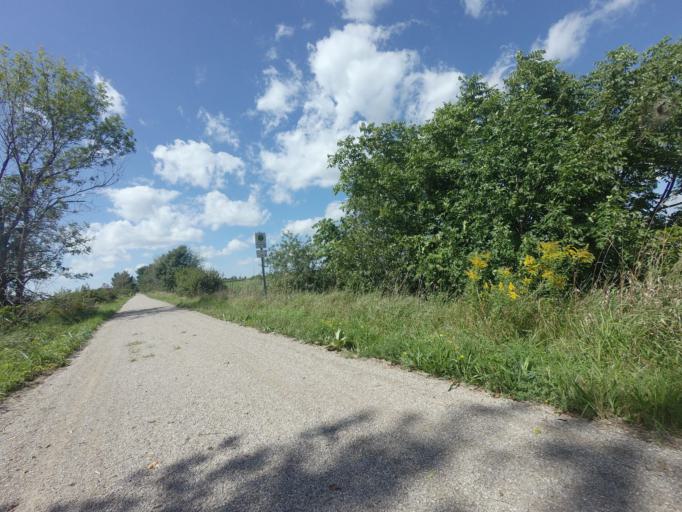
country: CA
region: Ontario
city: Huron East
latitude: 43.6701
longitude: -81.2749
